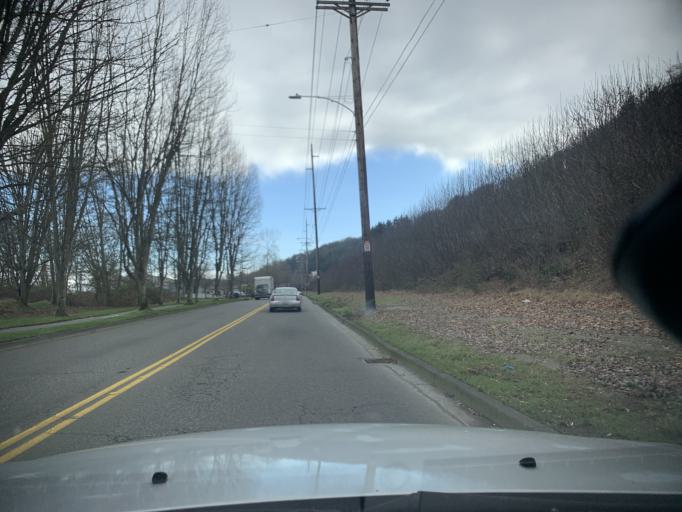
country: US
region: Washington
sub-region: Pierce County
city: Fircrest
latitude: 47.2904
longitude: -122.4928
